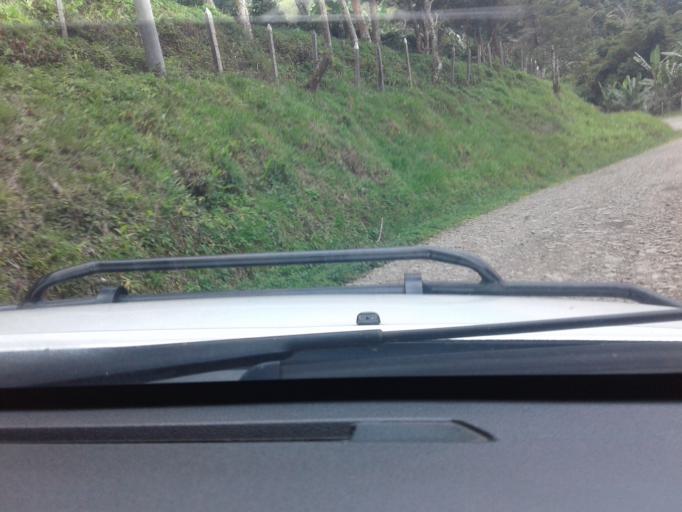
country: NI
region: Jinotega
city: Jinotega
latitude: 13.0709
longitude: -85.8805
